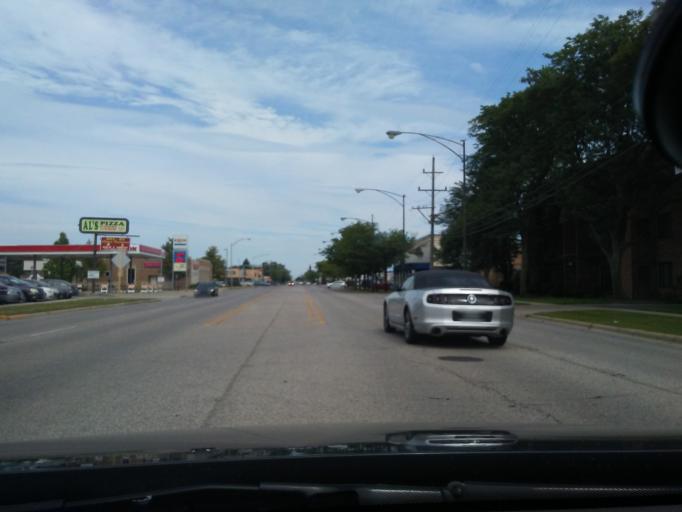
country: US
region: Illinois
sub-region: Cook County
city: Norridge
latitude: 41.9665
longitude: -87.8392
